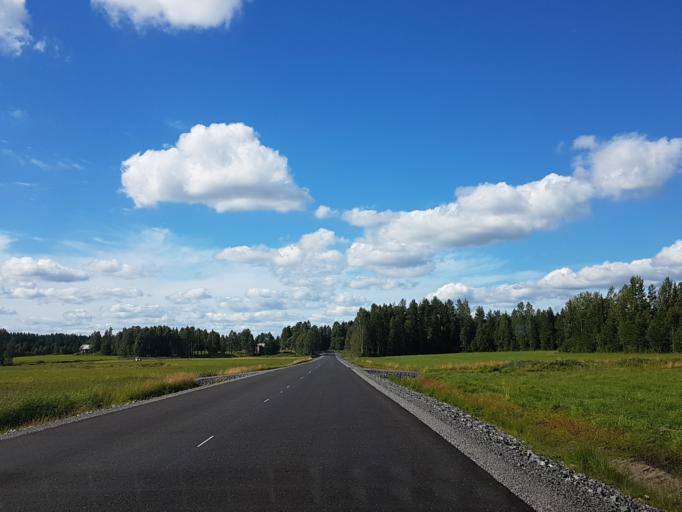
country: SE
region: Vaesterbotten
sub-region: Robertsfors Kommun
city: Robertsfors
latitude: 64.1351
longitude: 20.6326
